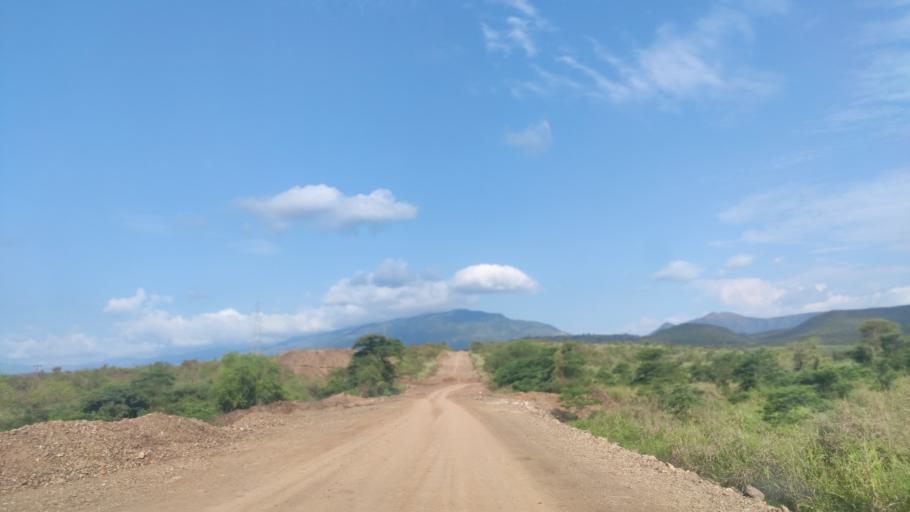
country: ET
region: Southern Nations, Nationalities, and People's Region
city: Felege Neway
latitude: 6.4343
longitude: 37.2696
